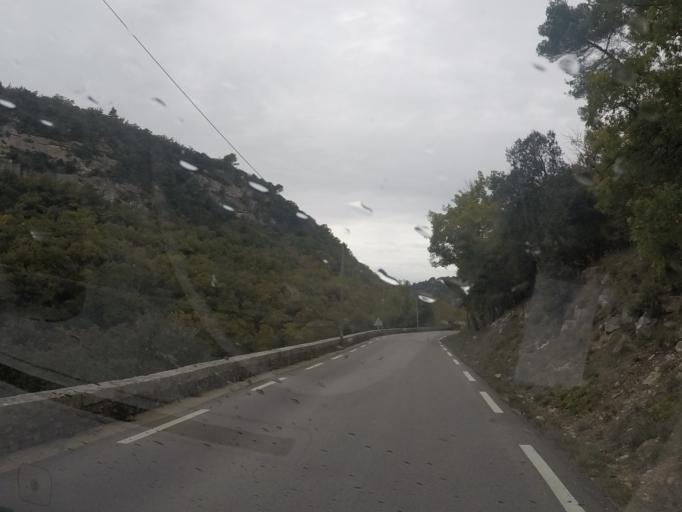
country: FR
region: Provence-Alpes-Cote d'Azur
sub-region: Departement du Vaucluse
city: Bonnieux
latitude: 43.8109
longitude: 5.3413
